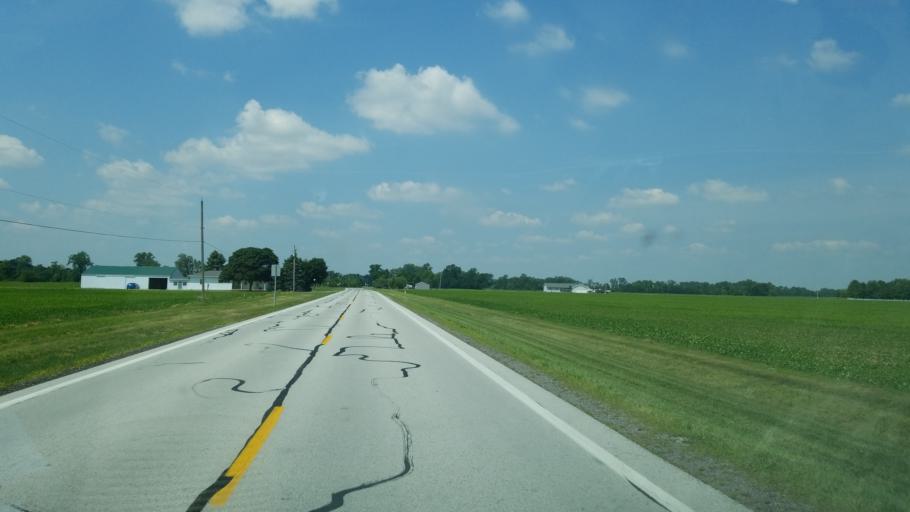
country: US
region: Ohio
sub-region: Henry County
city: Deshler
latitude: 41.2845
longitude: -83.8784
